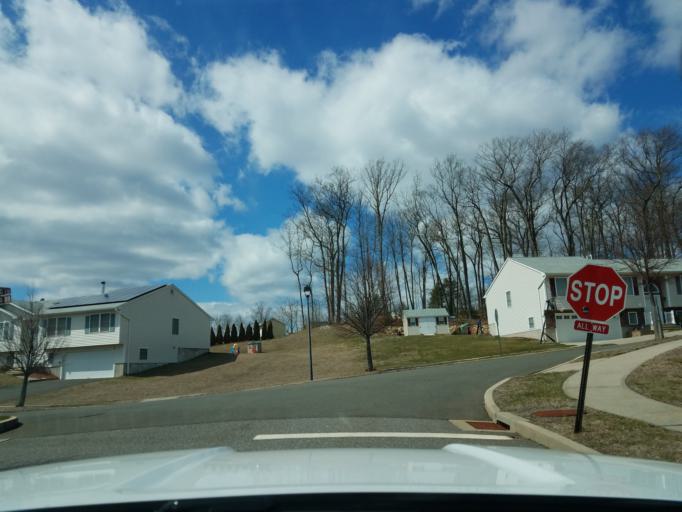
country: US
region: Connecticut
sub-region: New Haven County
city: Naugatuck
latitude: 41.4739
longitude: -73.0263
